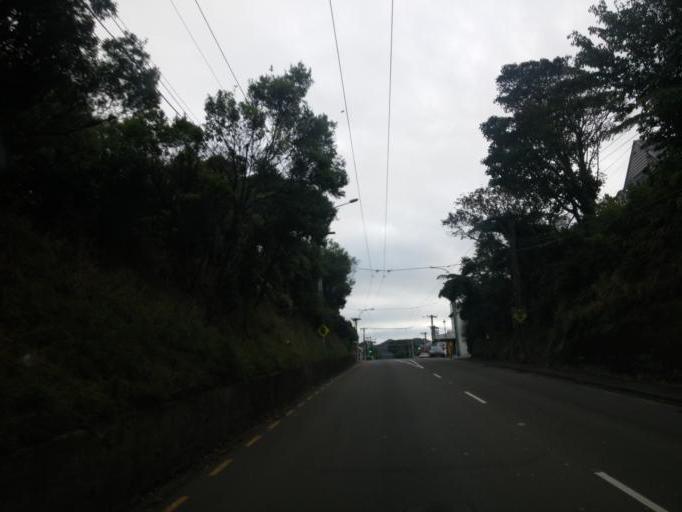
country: NZ
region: Wellington
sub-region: Wellington City
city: Kelburn
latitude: -41.2820
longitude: 174.7474
